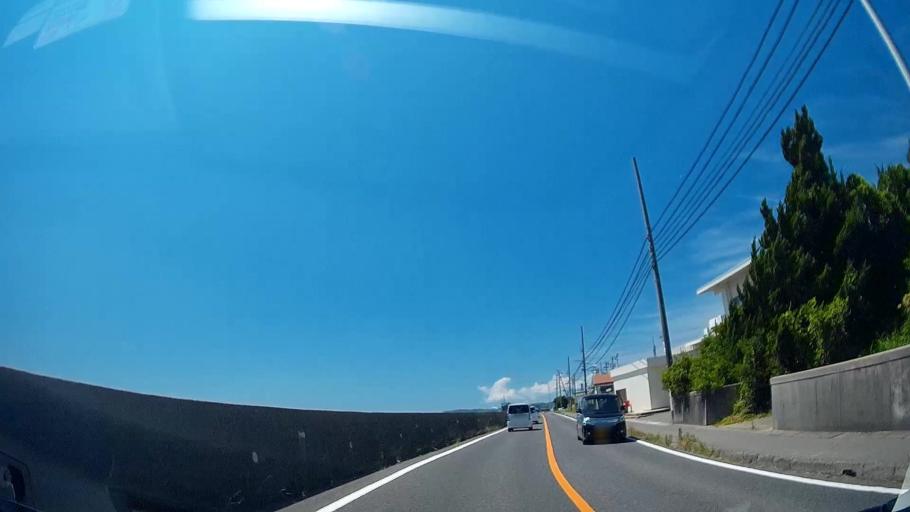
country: JP
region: Aichi
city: Taketoyo
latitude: 34.7948
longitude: 136.9210
